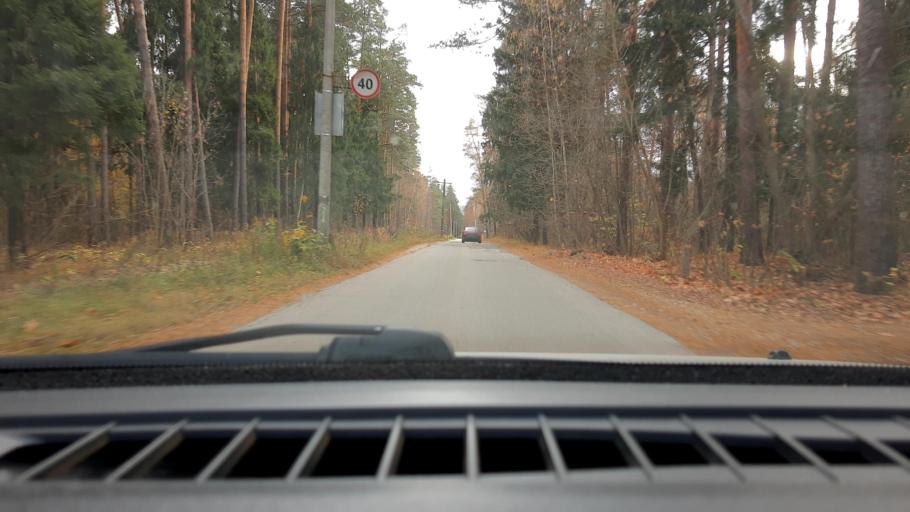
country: RU
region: Nizjnij Novgorod
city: Afonino
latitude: 56.1728
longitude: 44.0976
